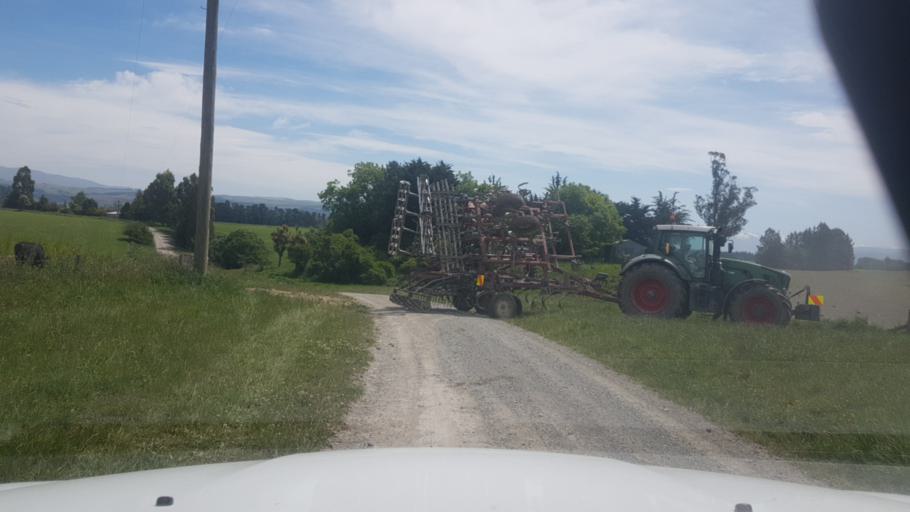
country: NZ
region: Canterbury
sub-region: Timaru District
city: Pleasant Point
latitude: -44.1672
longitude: 171.0145
